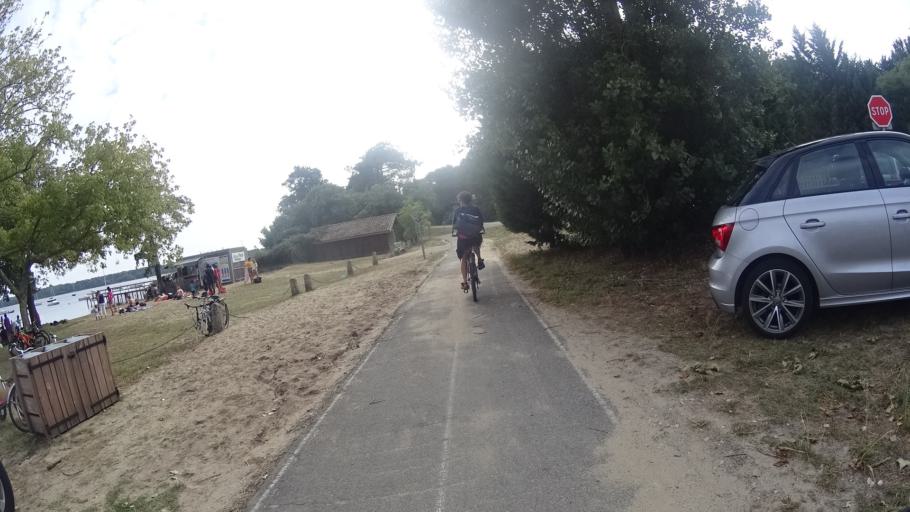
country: FR
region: Aquitaine
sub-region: Departement de la Gironde
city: Lacanau
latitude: 45.0016
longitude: -1.1371
